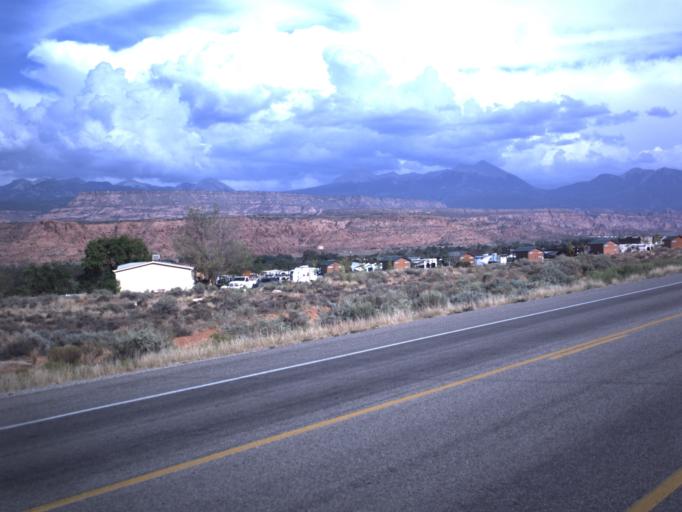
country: US
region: Utah
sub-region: Grand County
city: Moab
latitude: 38.5235
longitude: -109.4987
